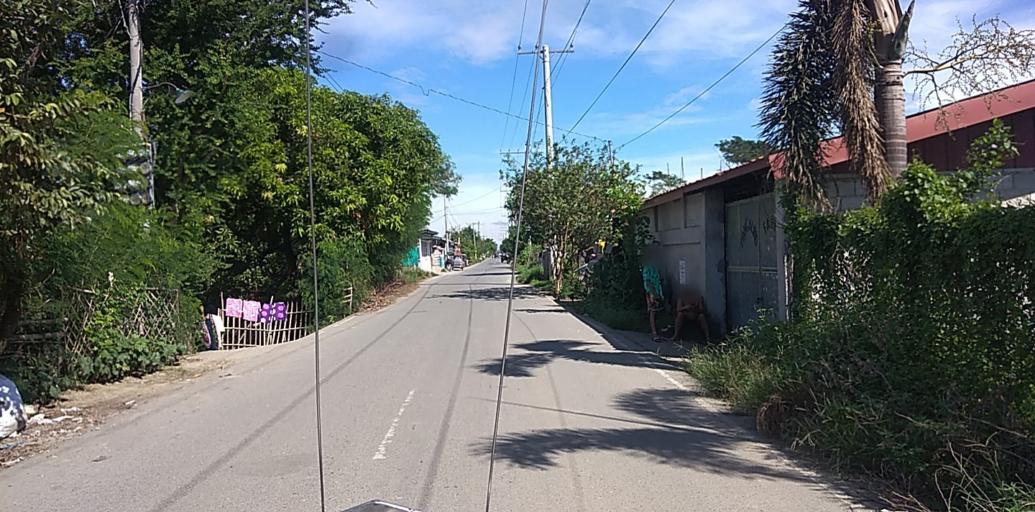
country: PH
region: Central Luzon
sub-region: Province of Pampanga
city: Candaba
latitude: 15.0839
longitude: 120.8097
